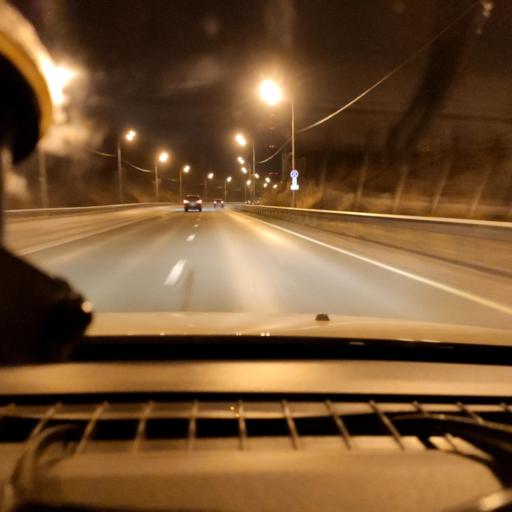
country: RU
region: Samara
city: Samara
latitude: 53.3006
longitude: 50.2260
